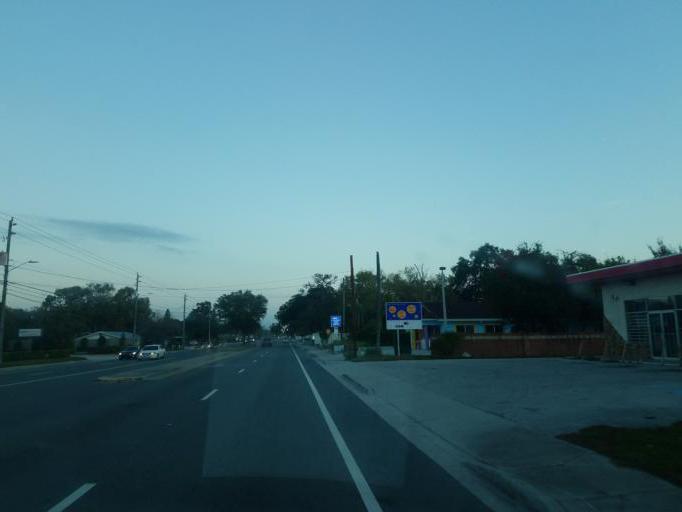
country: US
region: Florida
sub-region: Sarasota County
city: Kensington Park
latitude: 27.3671
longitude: -82.5056
